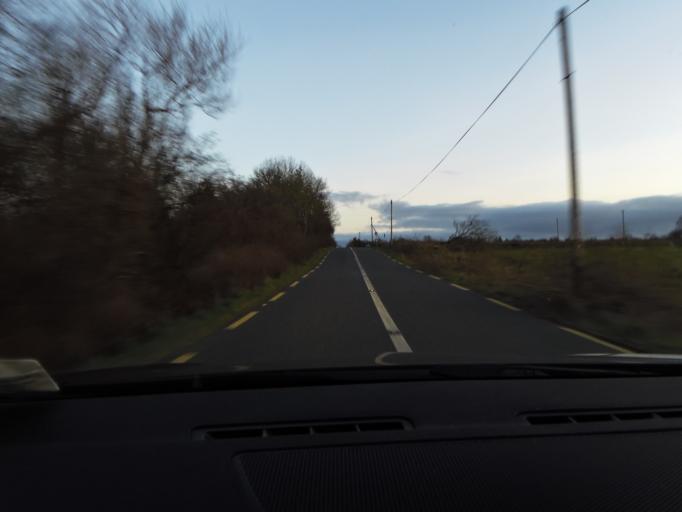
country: IE
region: Connaught
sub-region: Roscommon
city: Boyle
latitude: 53.8952
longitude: -8.2510
